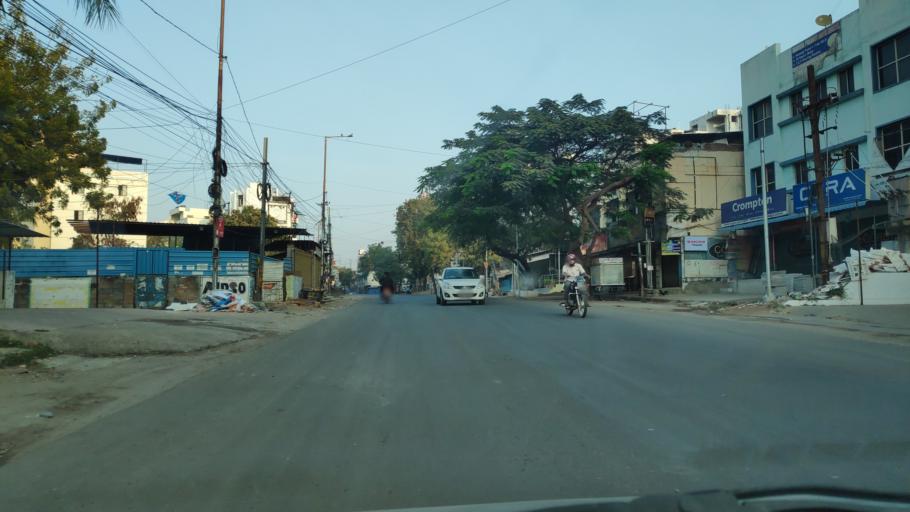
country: IN
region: Telangana
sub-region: Rangareddi
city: Gaddi Annaram
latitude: 17.3670
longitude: 78.5204
